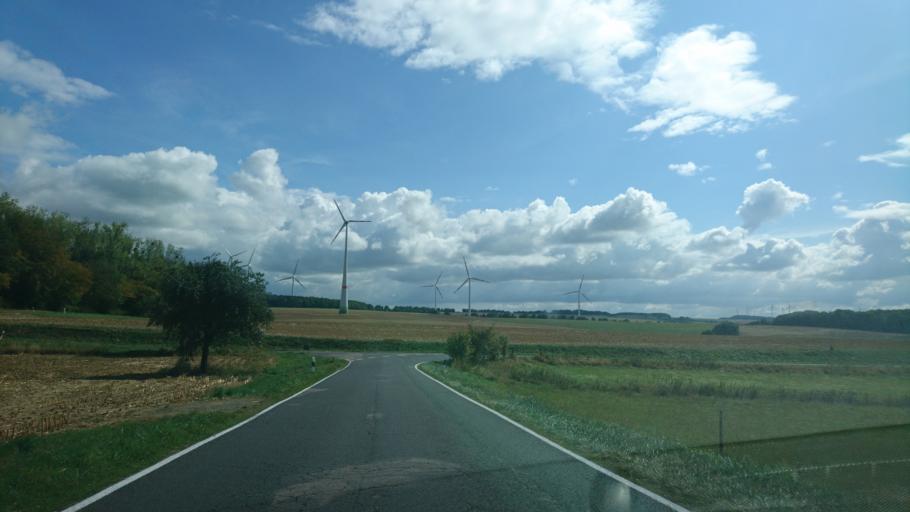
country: DE
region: Rheinland-Pfalz
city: Merzkirchen
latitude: 49.5704
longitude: 6.4629
